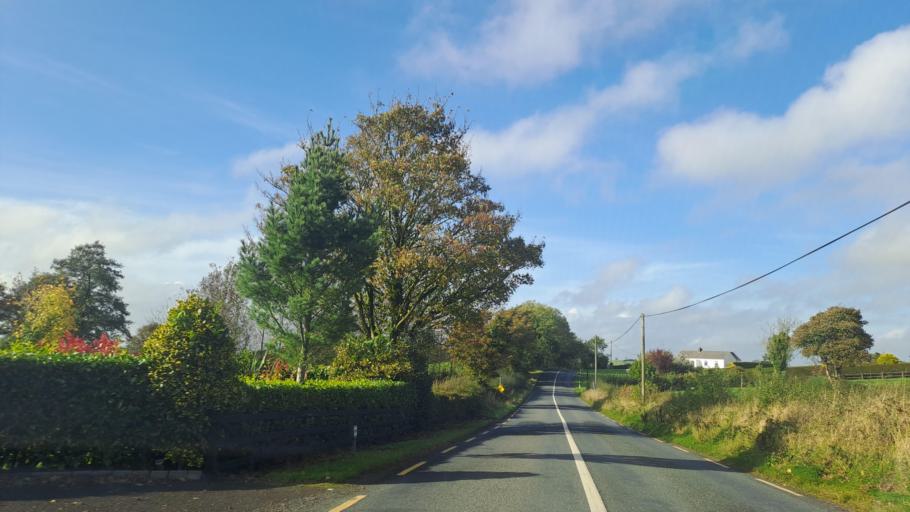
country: IE
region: Ulster
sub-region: An Cabhan
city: Cootehill
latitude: 54.0582
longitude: -7.0268
